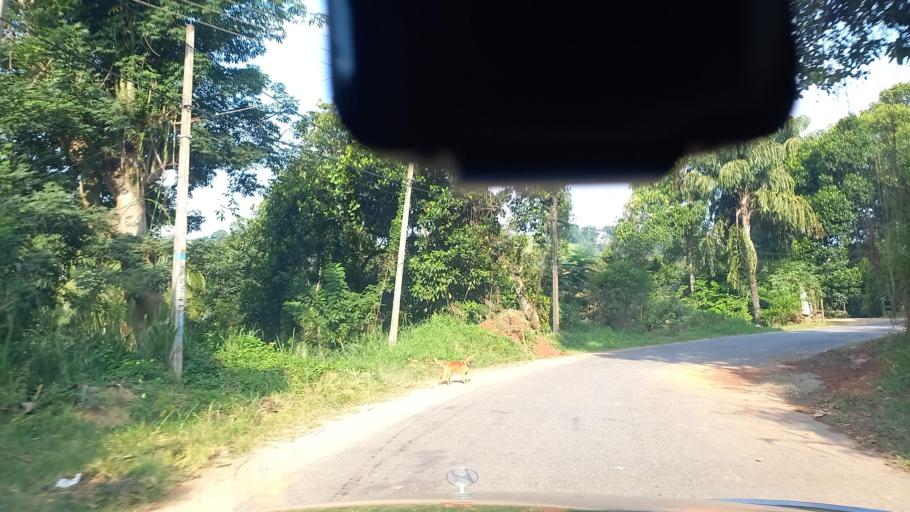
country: LK
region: Central
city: Gampola
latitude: 7.2251
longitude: 80.6046
